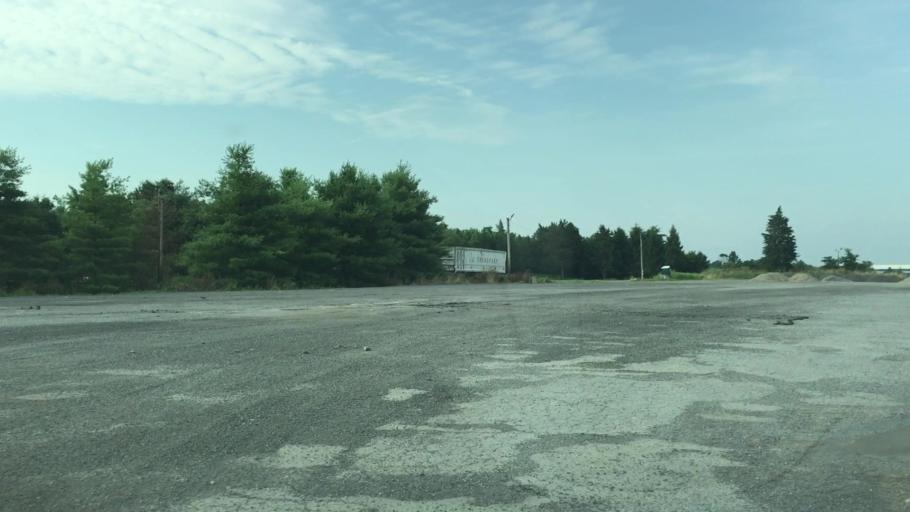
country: US
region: Pennsylvania
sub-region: Franklin County
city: State Line
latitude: 39.7181
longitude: -77.7183
